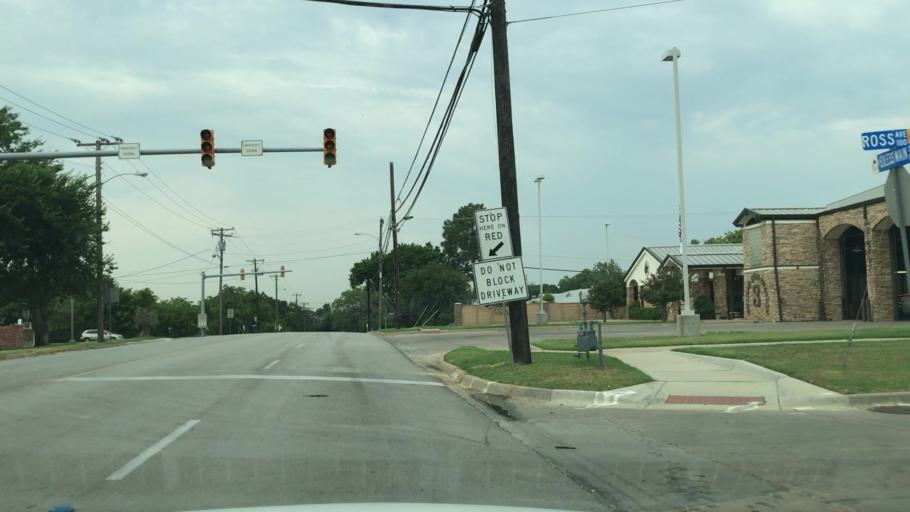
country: US
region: Texas
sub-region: Tarrant County
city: Euless
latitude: 32.8359
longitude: -97.0827
